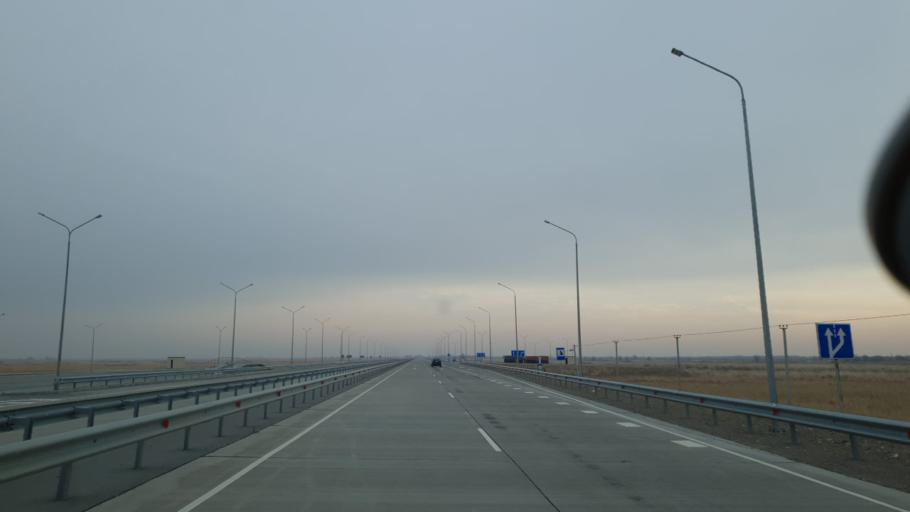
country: KZ
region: Almaty Oblysy
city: Zharkent
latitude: 44.0184
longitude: 79.7012
